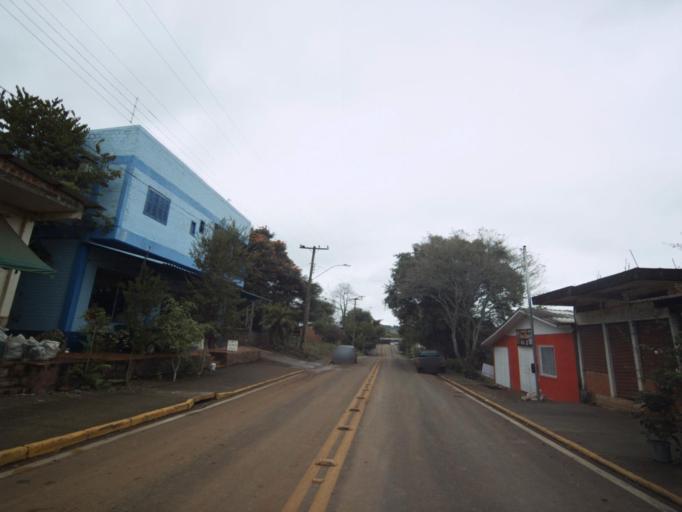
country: AR
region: Misiones
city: El Soberbio
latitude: -27.2960
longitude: -54.1900
